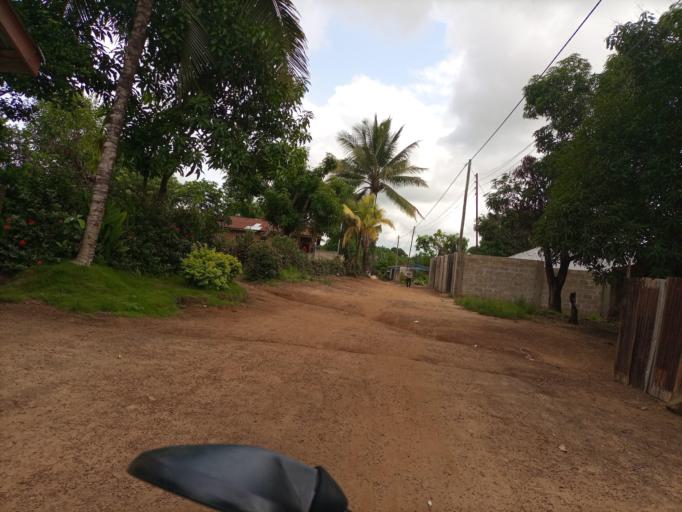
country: SL
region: Southern Province
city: Bo
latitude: 7.9648
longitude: -11.7598
